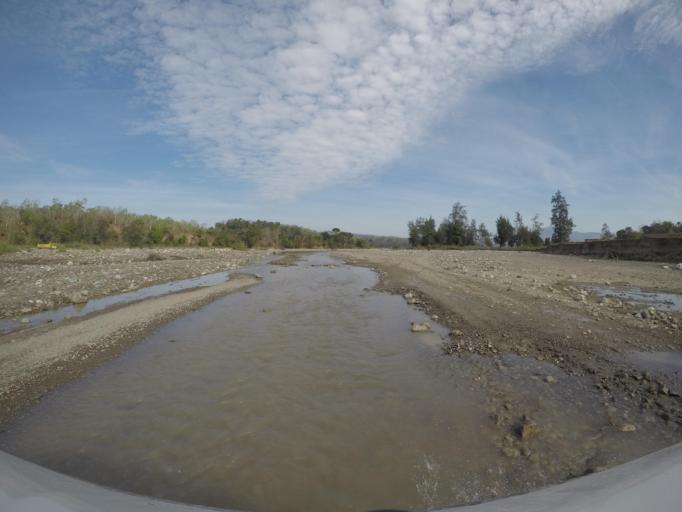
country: TL
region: Bobonaro
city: Maliana
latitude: -8.9051
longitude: 125.2112
